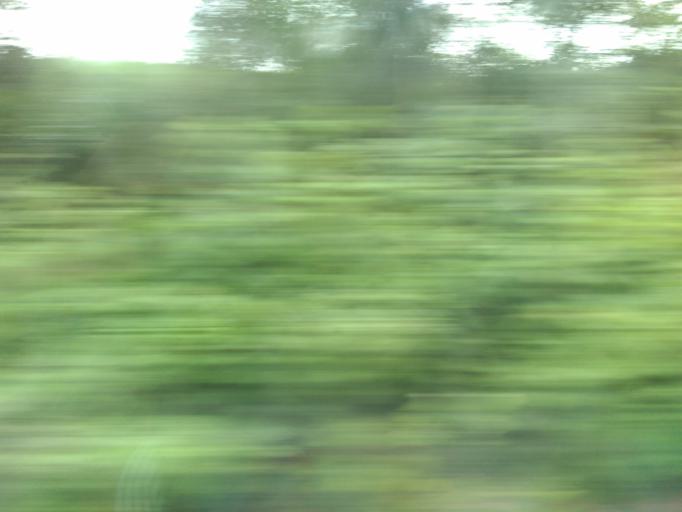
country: GB
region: Scotland
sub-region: East Lothian
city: Musselburgh
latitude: 55.9456
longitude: -3.0940
